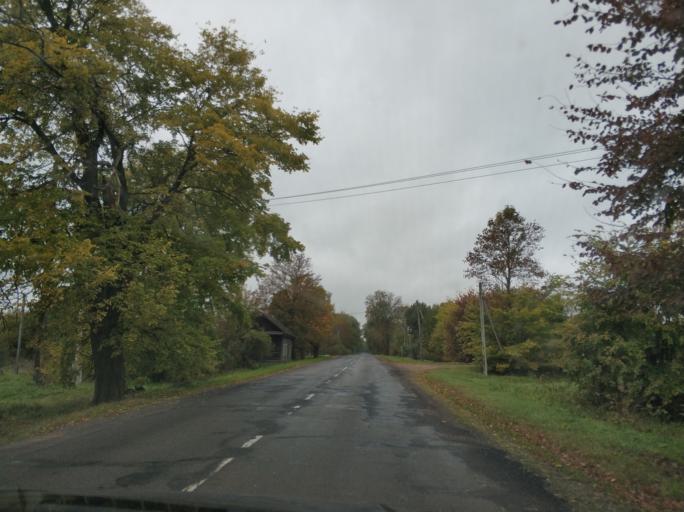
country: BY
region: Vitebsk
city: Polatsk
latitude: 55.4305
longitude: 28.9968
